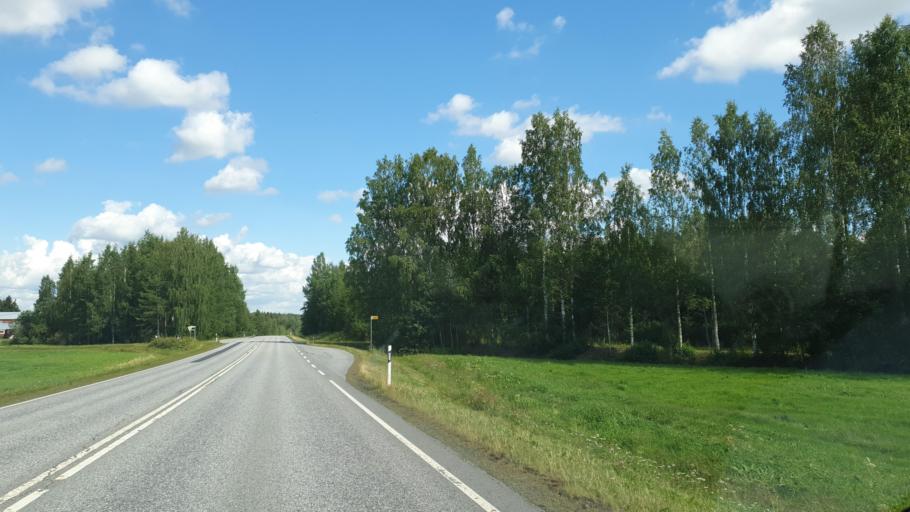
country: FI
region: Northern Savo
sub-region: Ylae-Savo
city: Sonkajaervi
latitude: 63.7513
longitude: 27.3869
